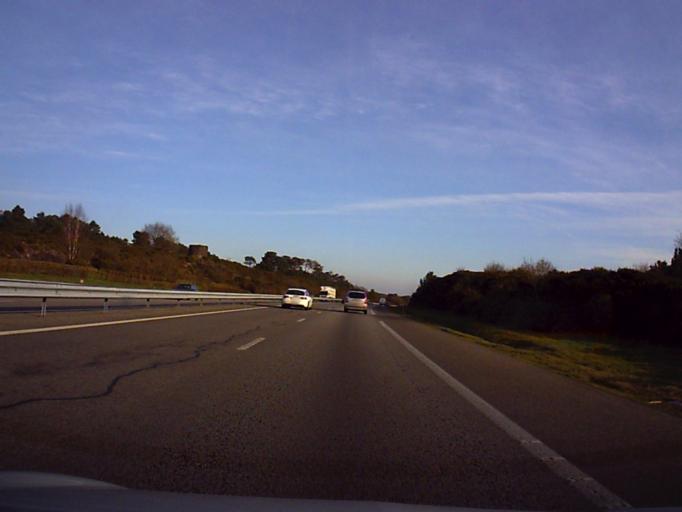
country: FR
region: Brittany
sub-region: Departement du Morbihan
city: Augan
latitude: 47.9383
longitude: -2.2597
